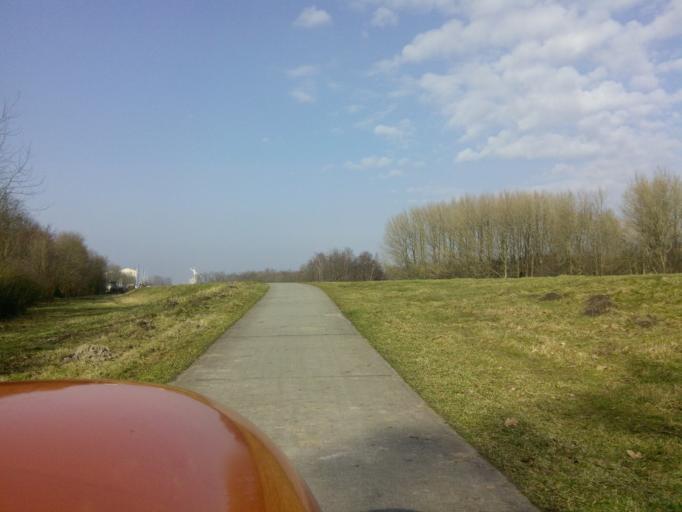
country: NL
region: Utrecht
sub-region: Gemeente Bunschoten
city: Bunschoten
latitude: 52.2553
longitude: 5.4006
